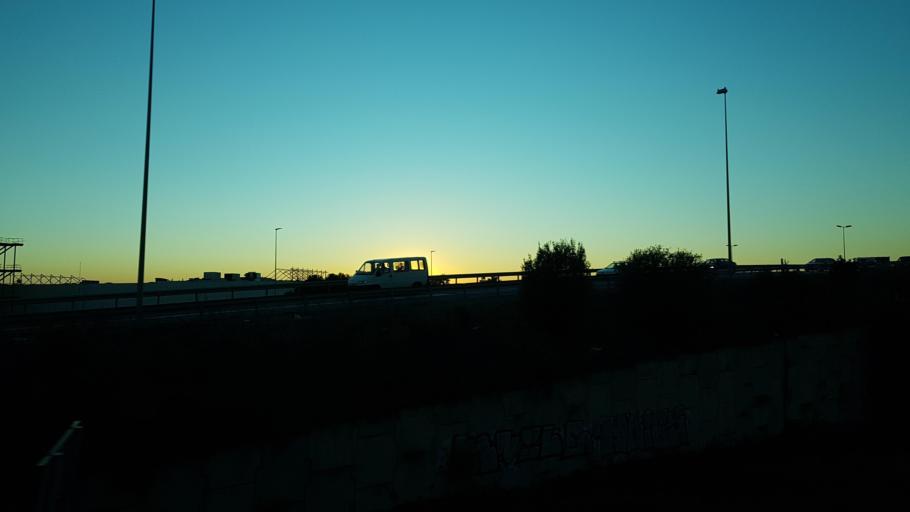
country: ES
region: Valencia
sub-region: Provincia de Valencia
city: Aldaia
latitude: 39.4749
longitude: -0.4837
